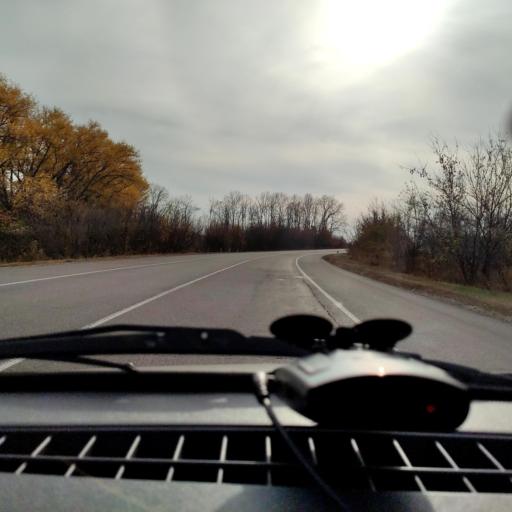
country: RU
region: Voronezj
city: Devitsa
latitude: 51.5953
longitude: 38.9769
